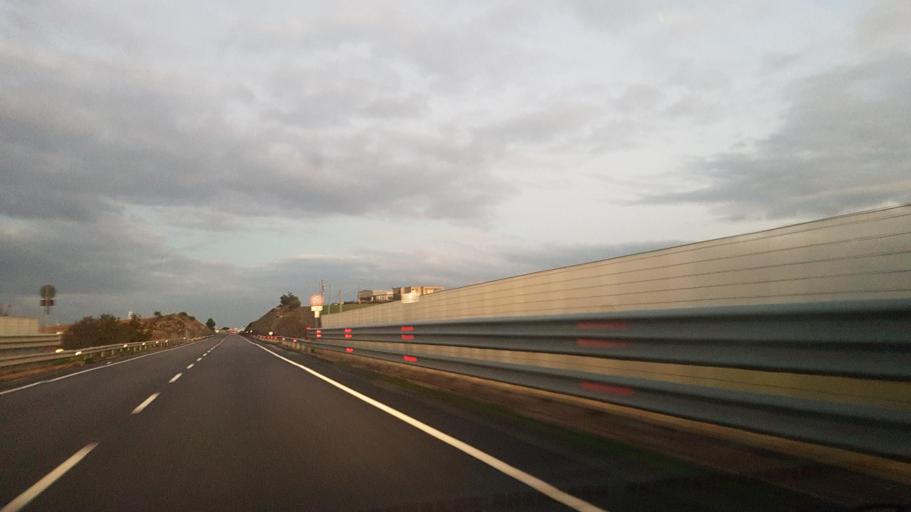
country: IT
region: Apulia
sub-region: Provincia di Taranto
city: Laterza
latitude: 40.6575
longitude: 16.7747
